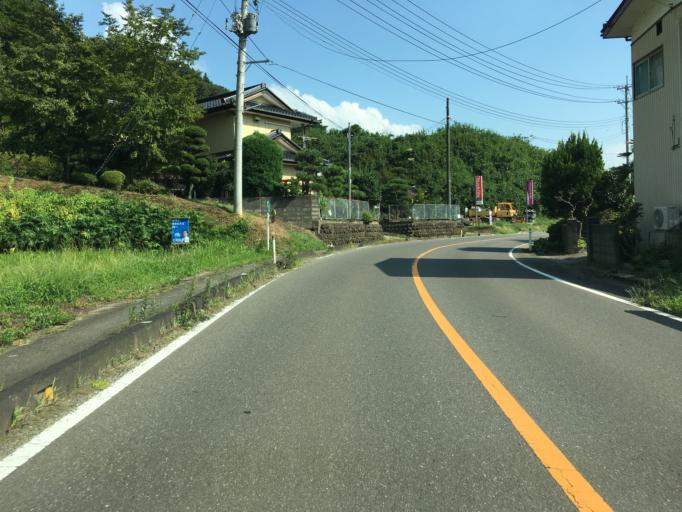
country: JP
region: Fukushima
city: Nihommatsu
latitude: 37.5904
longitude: 140.4110
